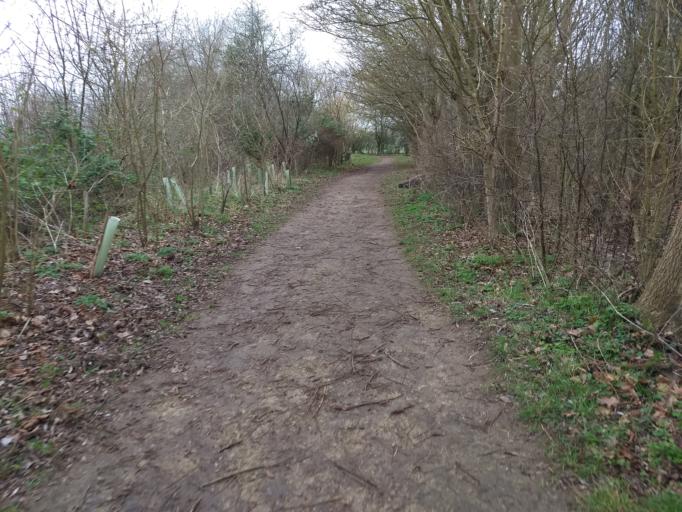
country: GB
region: England
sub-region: Bedford
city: Odell
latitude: 52.2062
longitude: -0.5905
